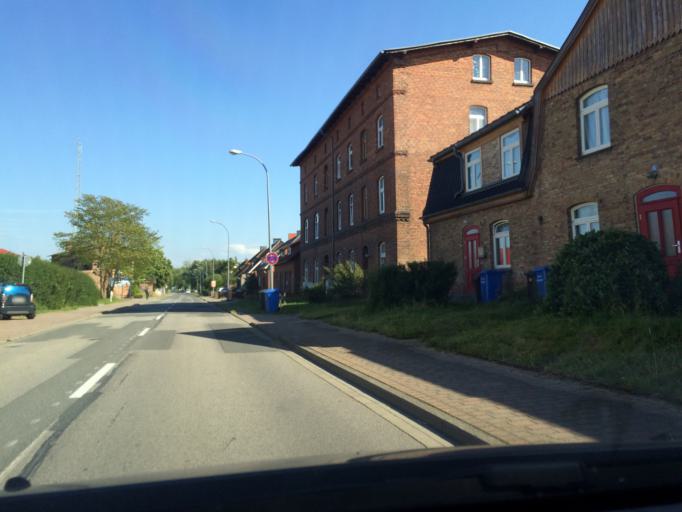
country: DE
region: Mecklenburg-Vorpommern
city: Barth
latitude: 54.3609
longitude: 12.7349
